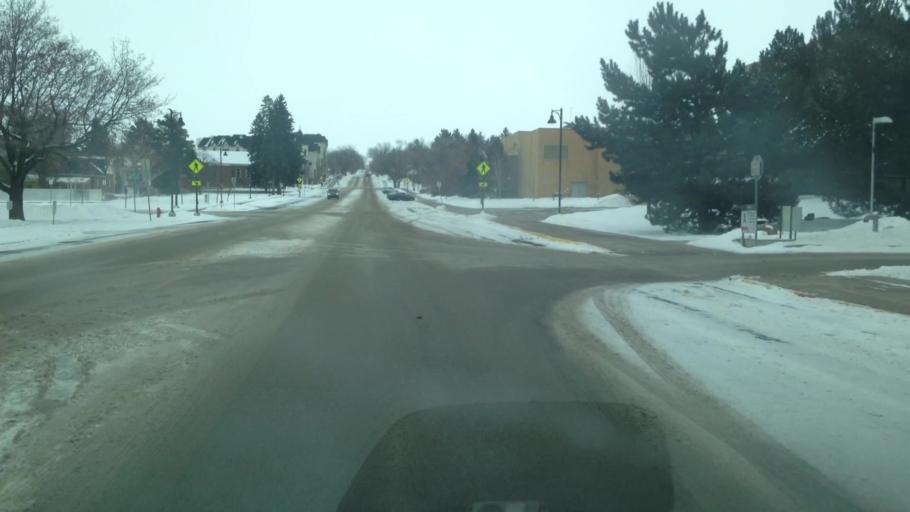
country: US
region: Idaho
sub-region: Madison County
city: Rexburg
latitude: 43.8219
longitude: -111.7849
